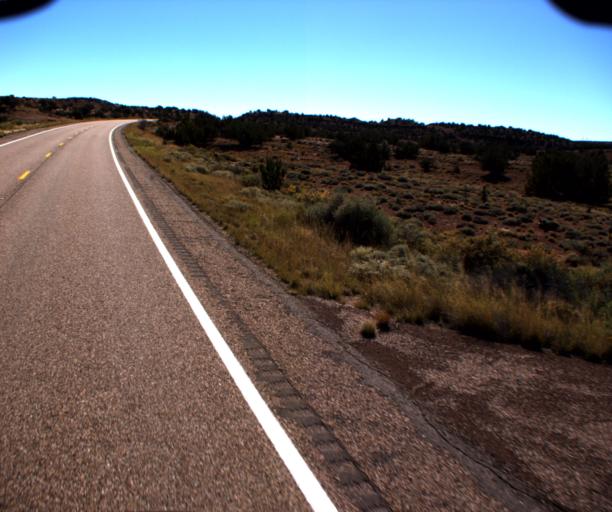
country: US
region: Arizona
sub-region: Apache County
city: Saint Johns
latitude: 34.5862
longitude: -109.5434
